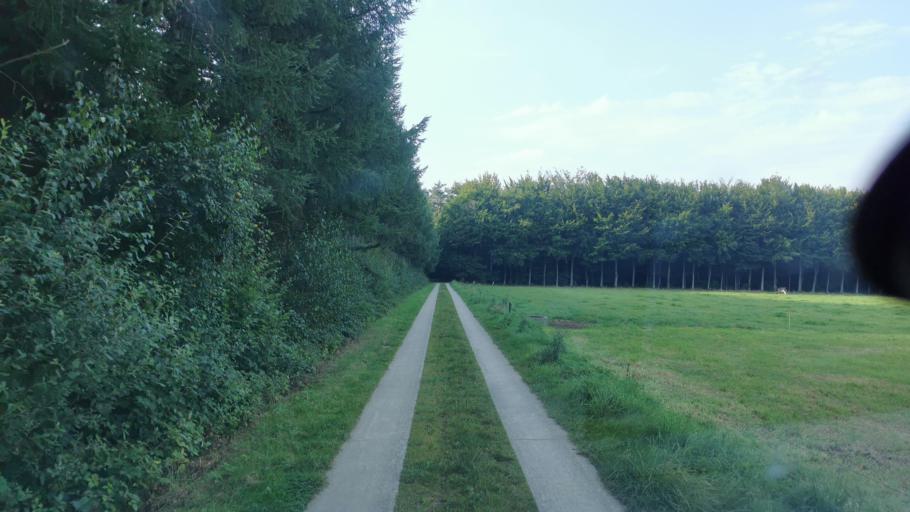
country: NL
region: Overijssel
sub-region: Gemeente Losser
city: Losser
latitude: 52.2902
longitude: 6.9730
